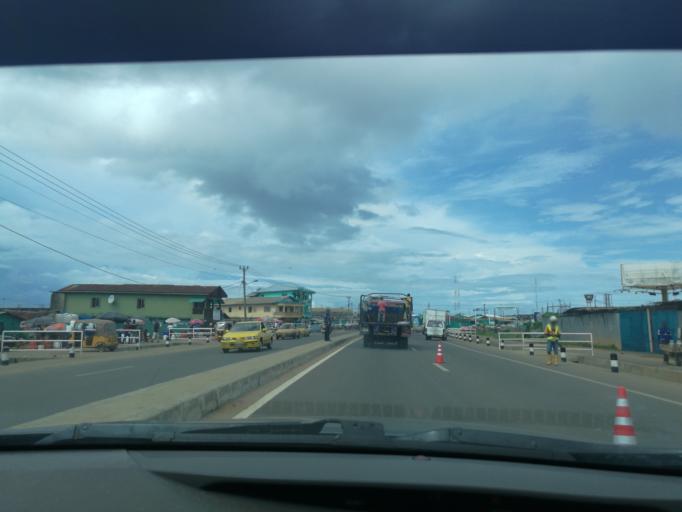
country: LR
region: Montserrado
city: Monrovia
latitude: 6.3375
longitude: -10.7917
